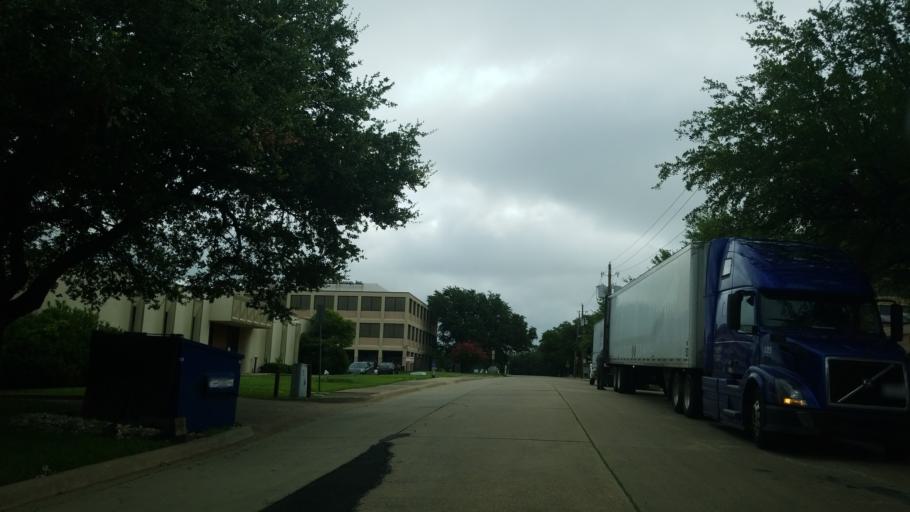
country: US
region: Texas
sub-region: Dallas County
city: University Park
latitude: 32.8336
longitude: -96.8709
